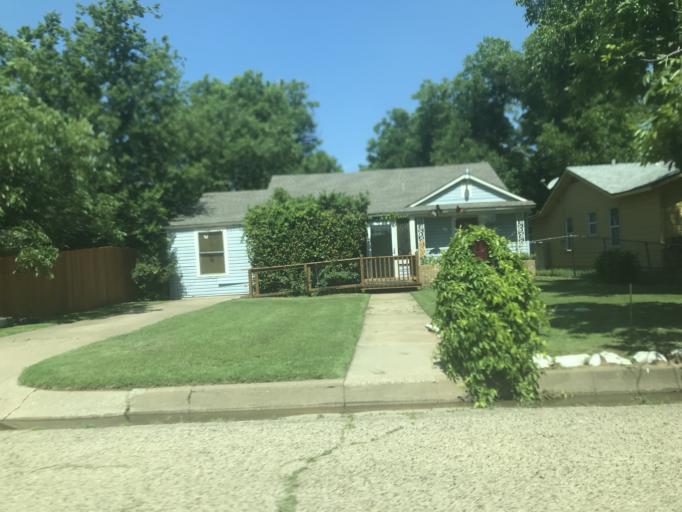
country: US
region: Texas
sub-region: Taylor County
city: Abilene
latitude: 32.4676
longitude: -99.7362
